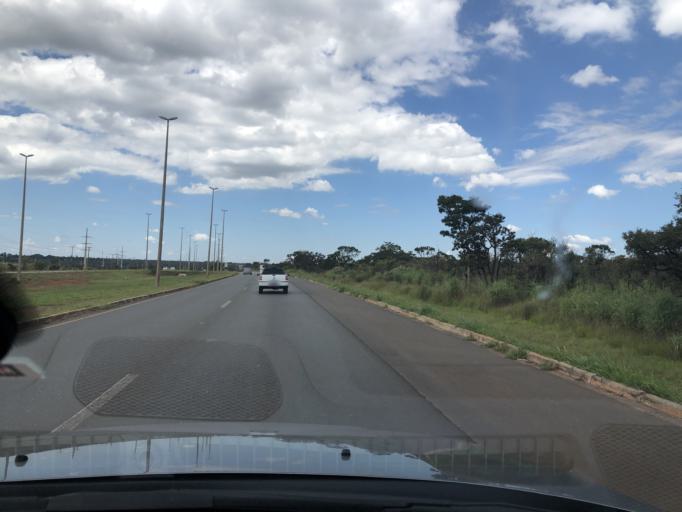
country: BR
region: Federal District
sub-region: Brasilia
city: Brasilia
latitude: -15.9716
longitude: -48.0161
